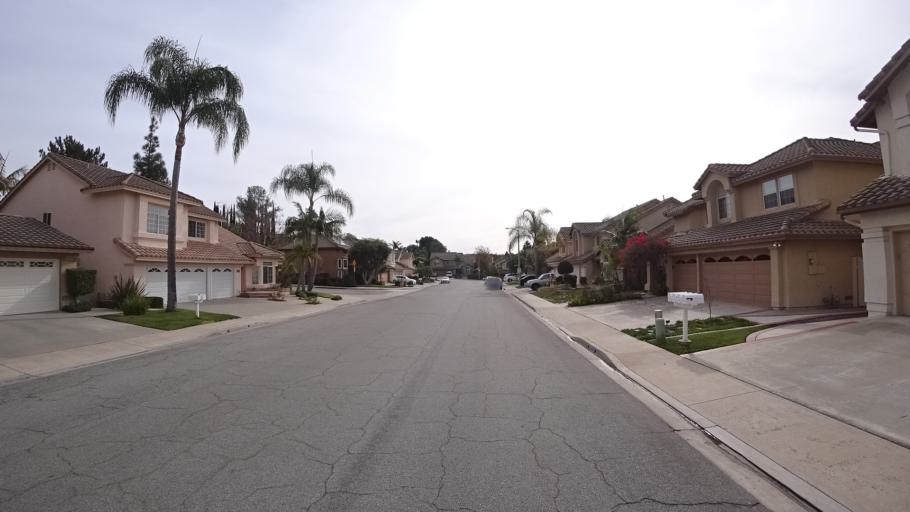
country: US
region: California
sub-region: Orange County
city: Laguna Woods
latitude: 33.5922
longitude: -117.7422
